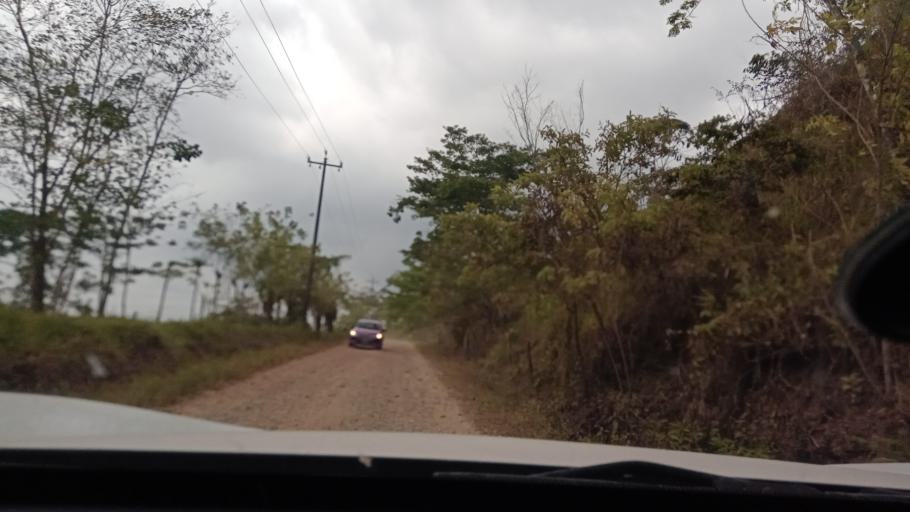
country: MX
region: Tabasco
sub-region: Huimanguillo
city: Francisco Rueda
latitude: 17.4332
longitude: -94.0470
